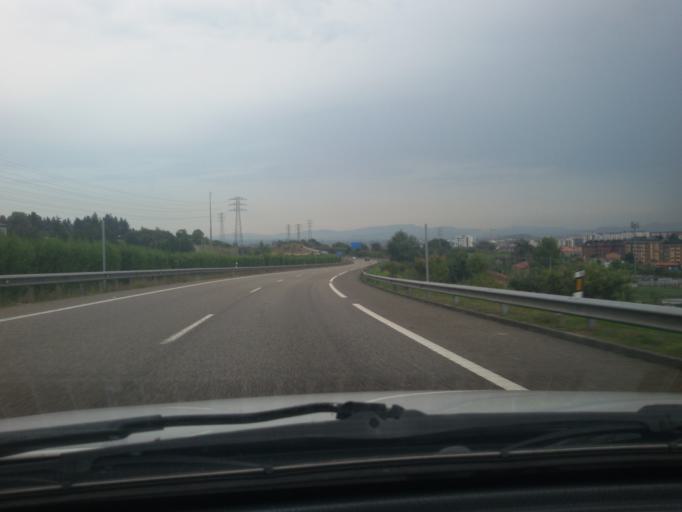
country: ES
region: Asturias
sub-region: Province of Asturias
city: Oviedo
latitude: 43.3794
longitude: -5.8387
